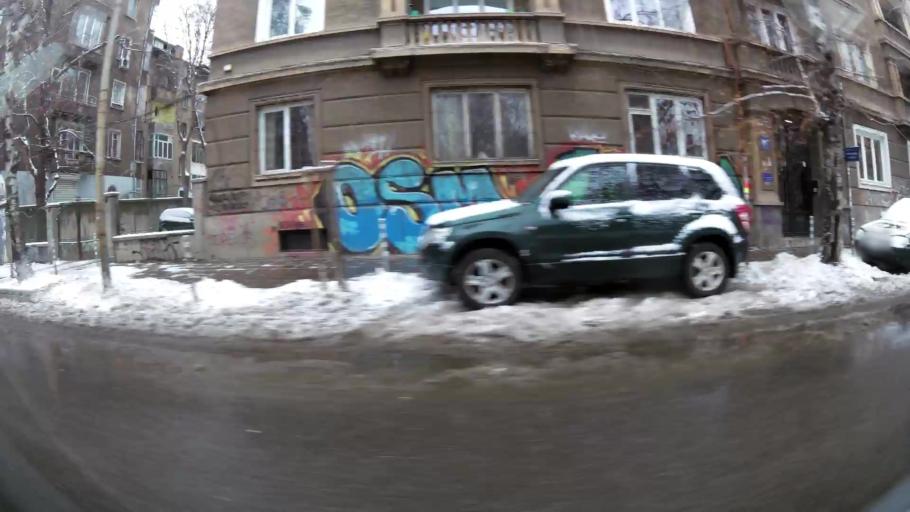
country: BG
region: Sofia-Capital
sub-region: Stolichna Obshtina
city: Sofia
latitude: 42.6916
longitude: 23.3408
